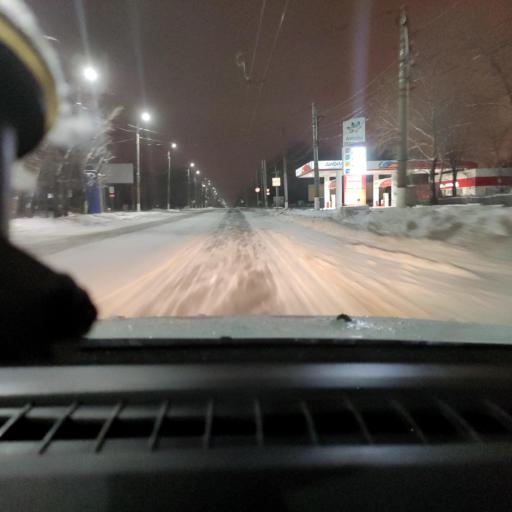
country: RU
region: Samara
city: Novokuybyshevsk
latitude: 53.0857
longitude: 49.9474
